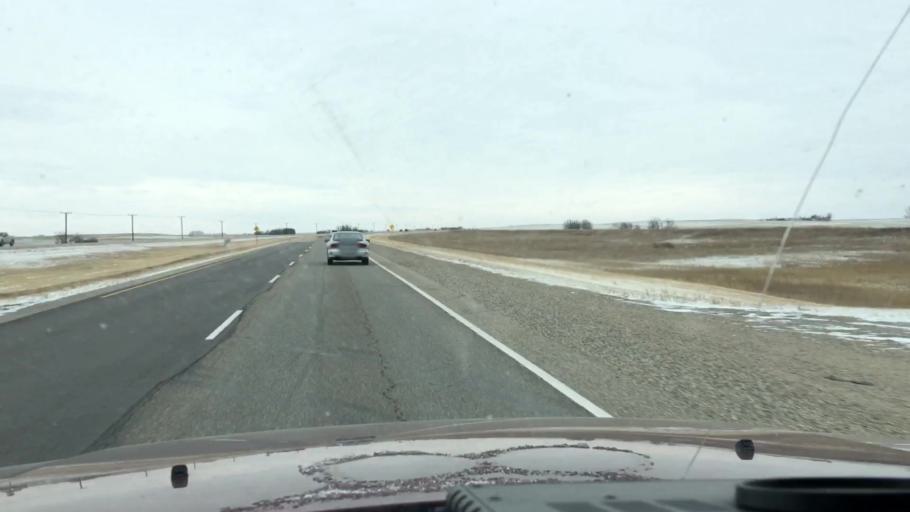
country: CA
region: Saskatchewan
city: Watrous
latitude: 51.4396
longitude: -106.2079
